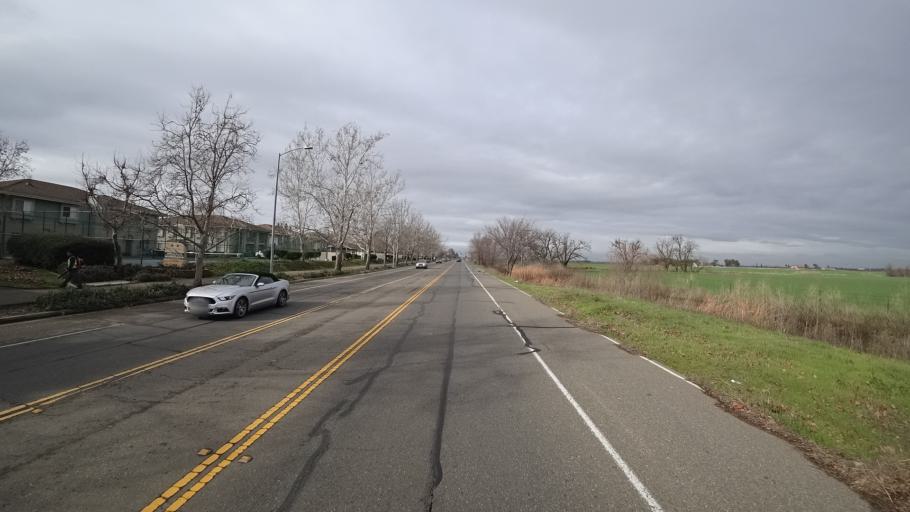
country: US
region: California
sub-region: Yolo County
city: Davis
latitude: 38.5610
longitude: -121.7755
